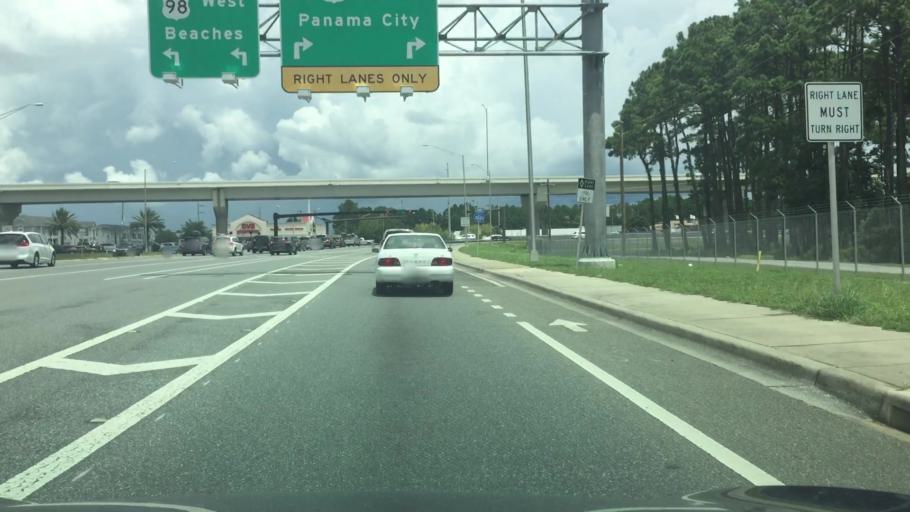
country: US
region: Florida
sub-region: Bay County
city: Upper Grand Lagoon
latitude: 30.1870
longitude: -85.7608
